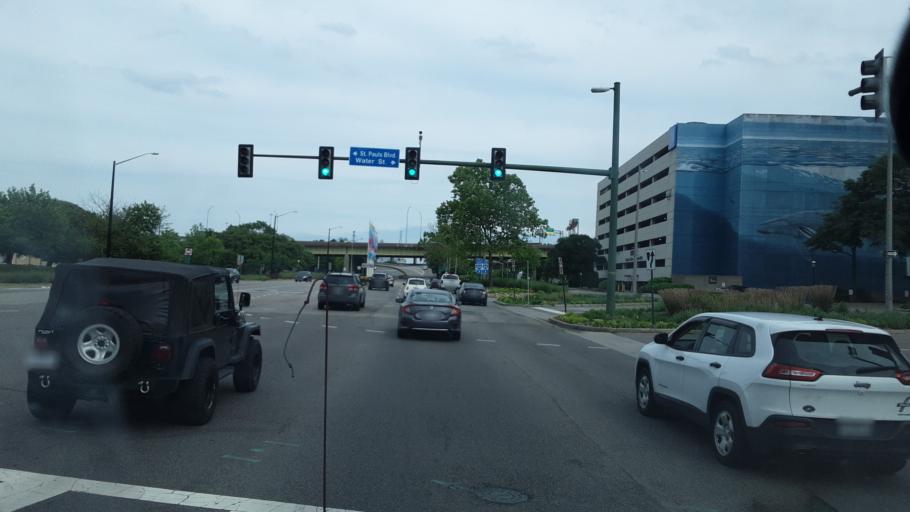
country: US
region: Virginia
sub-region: City of Norfolk
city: Norfolk
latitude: 36.8441
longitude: -76.2881
